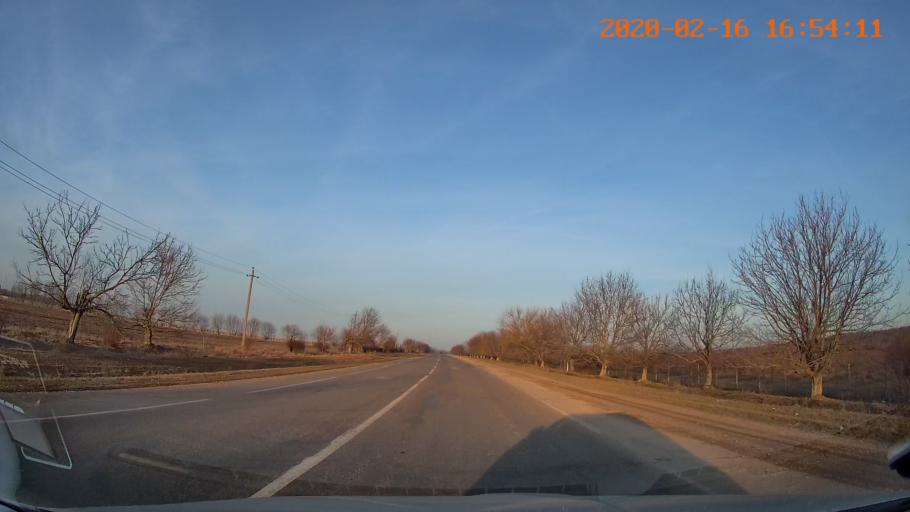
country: MD
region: Briceni
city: Briceni
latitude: 48.3181
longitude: 27.0020
